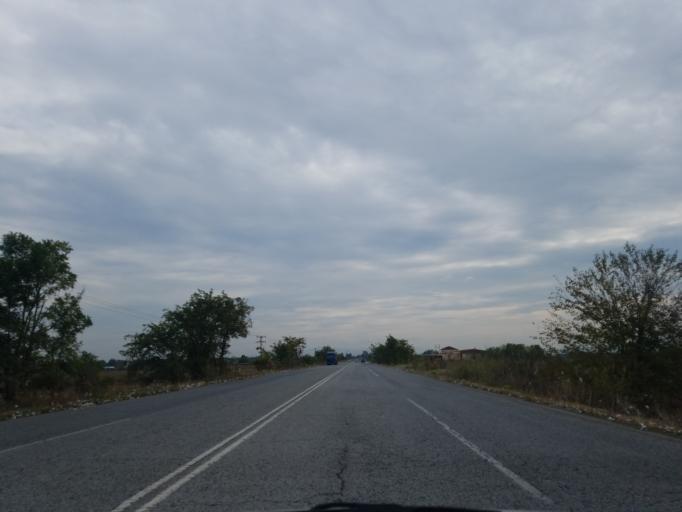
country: GR
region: Thessaly
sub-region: Nomos Kardhitsas
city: Sofades
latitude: 39.3478
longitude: 22.0711
